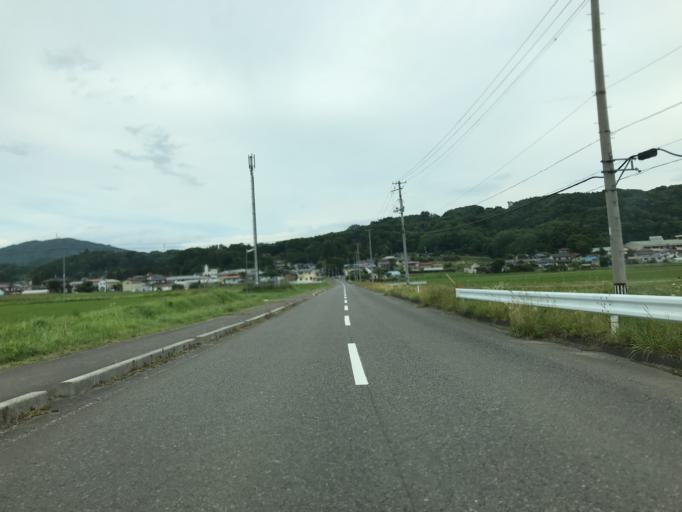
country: JP
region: Fukushima
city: Funehikimachi-funehiki
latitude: 37.3950
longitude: 140.5653
